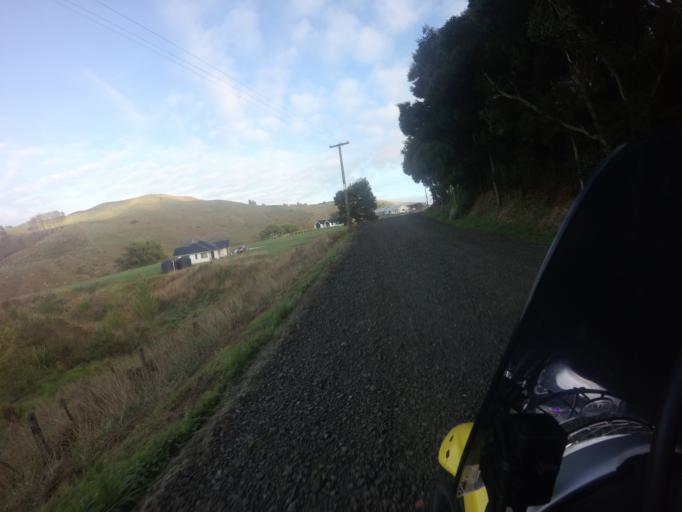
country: NZ
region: Gisborne
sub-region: Gisborne District
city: Gisborne
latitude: -38.6651
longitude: 178.0819
